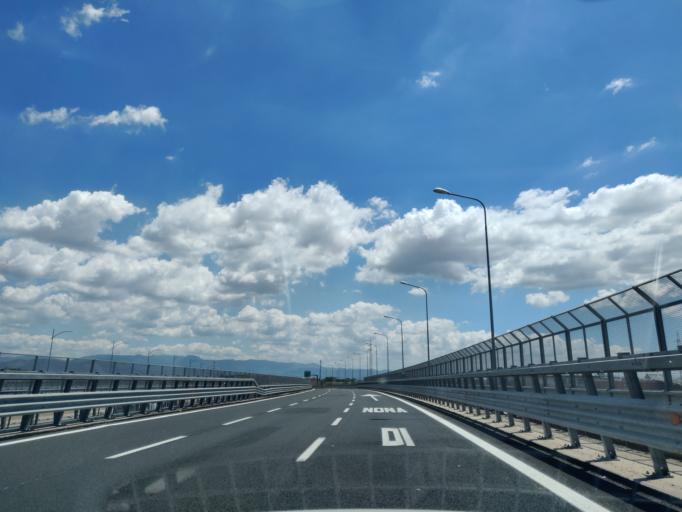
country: IT
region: Latium
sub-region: Citta metropolitana di Roma Capitale
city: Setteville
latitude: 41.9189
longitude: 12.6568
